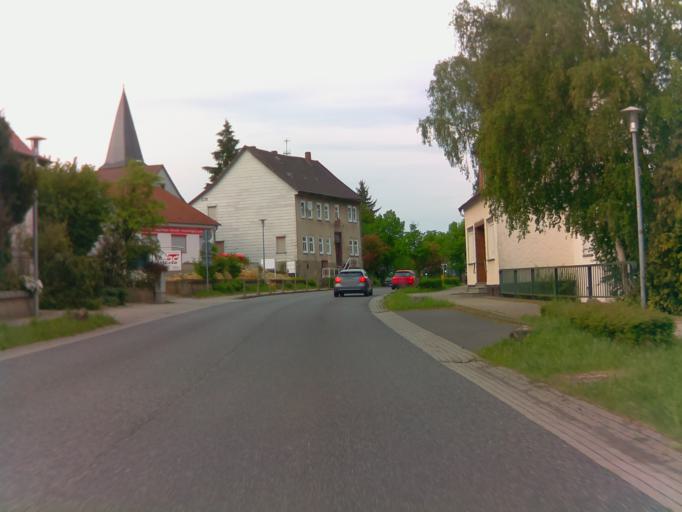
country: DE
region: Hesse
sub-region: Regierungsbezirk Kassel
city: Jesberg
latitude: 50.9954
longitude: 9.1437
